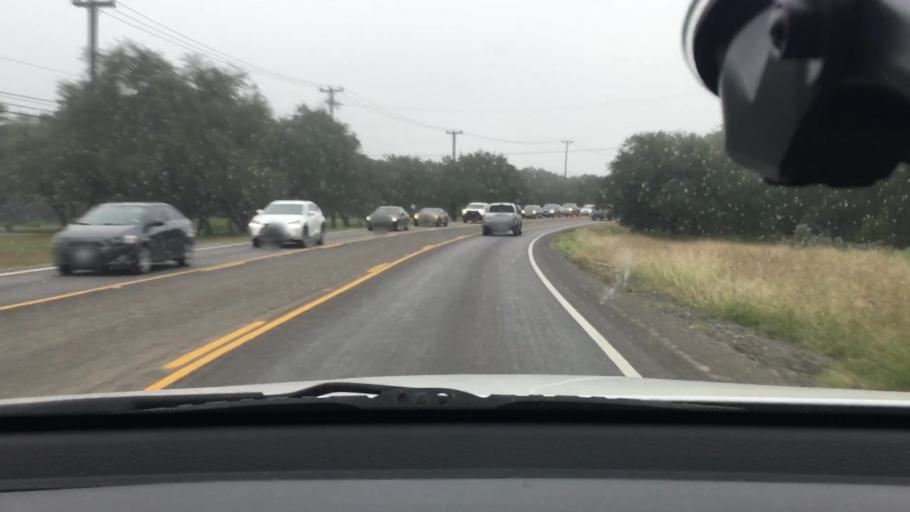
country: US
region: Texas
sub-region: Comal County
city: Garden Ridge
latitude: 29.6214
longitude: -98.3029
